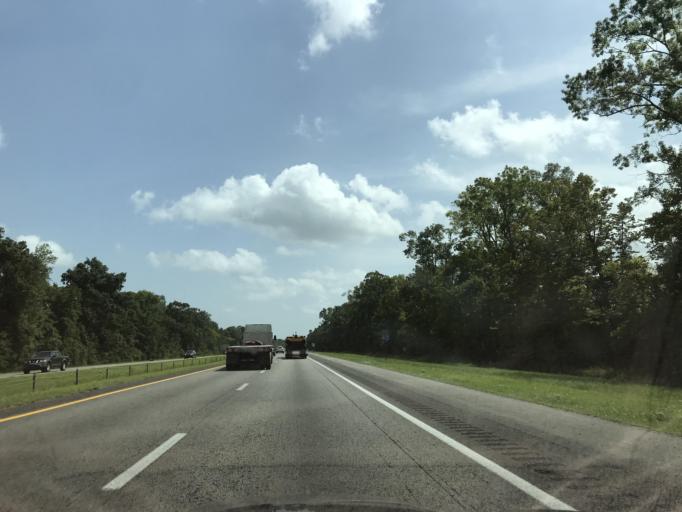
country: US
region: North Carolina
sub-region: Pender County
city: Rocky Point
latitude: 34.4327
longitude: -77.8721
